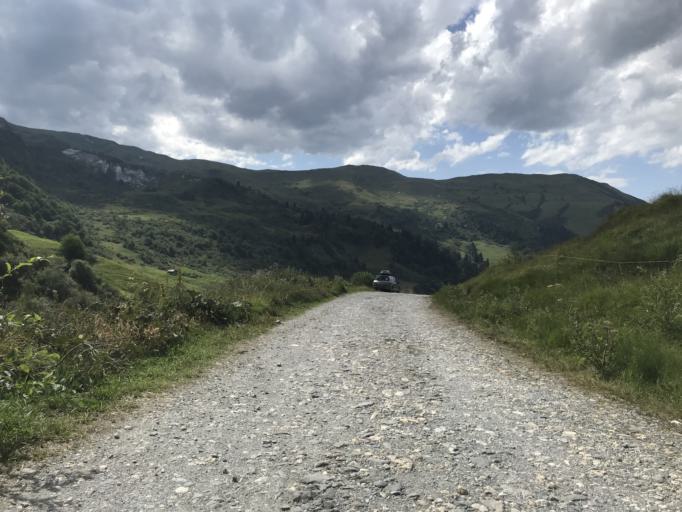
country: FR
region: Rhone-Alpes
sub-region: Departement de la Savoie
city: Beaufort
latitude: 45.6612
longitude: 6.6312
